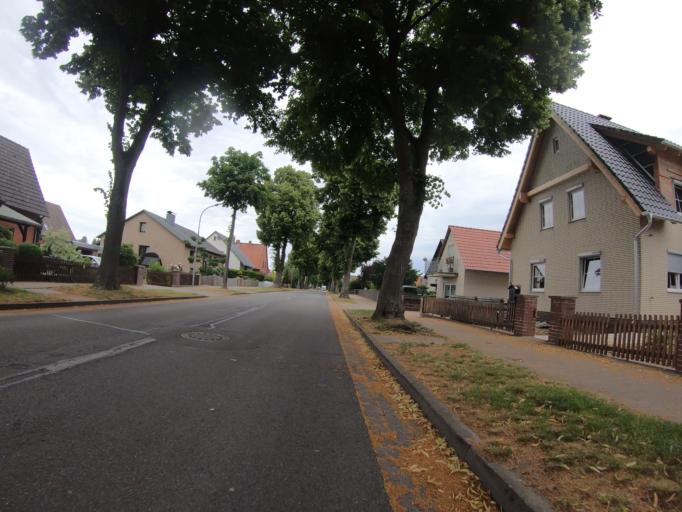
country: DE
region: Lower Saxony
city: Calberlah
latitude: 52.4224
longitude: 10.6231
